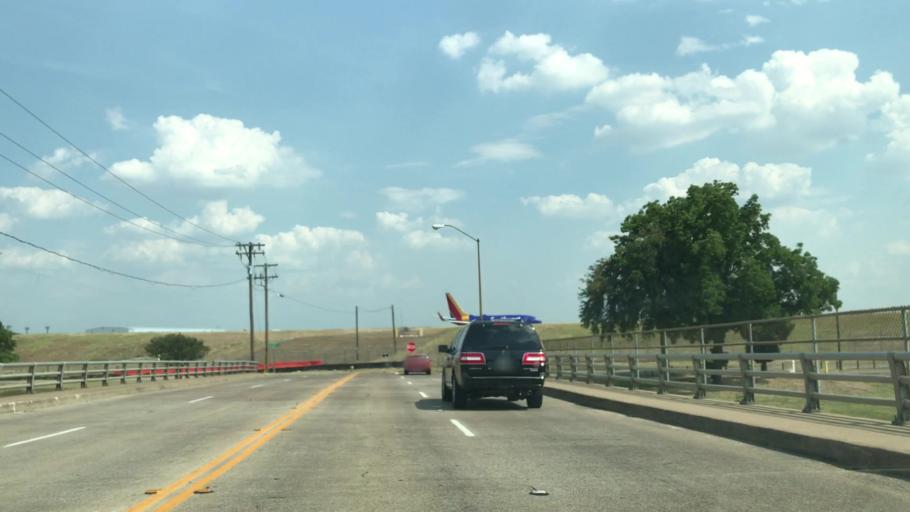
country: US
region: Texas
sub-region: Dallas County
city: University Park
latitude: 32.8597
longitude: -96.8565
